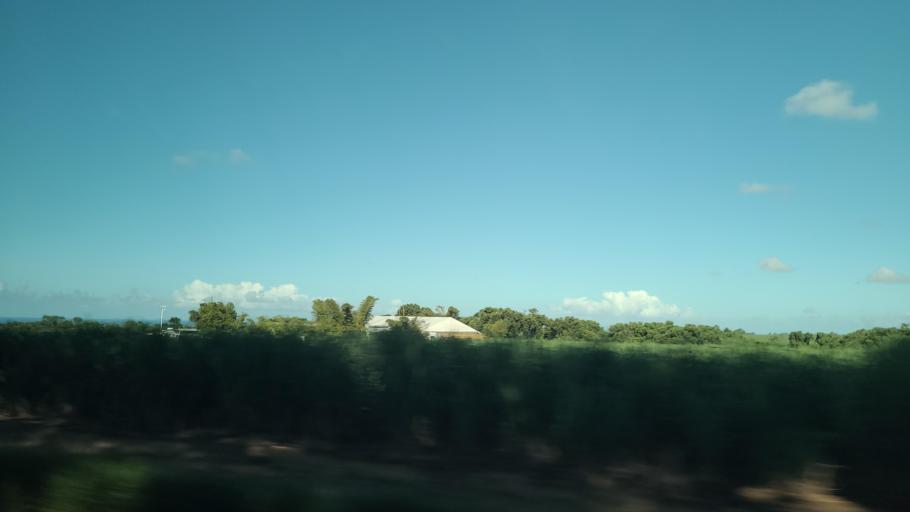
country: MU
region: Flacq
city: Centre de Flacq
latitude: -20.1994
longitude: 57.6948
